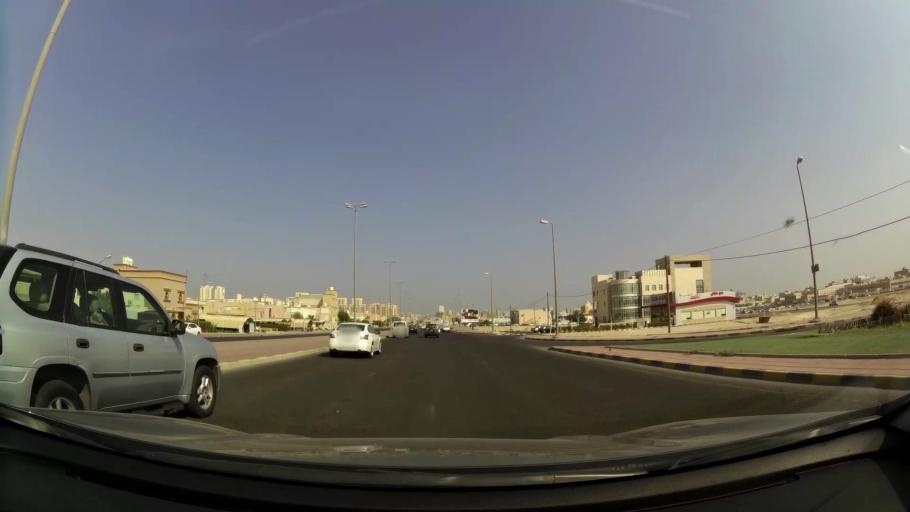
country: KW
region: Al Ahmadi
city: Ar Riqqah
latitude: 29.1348
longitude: 48.1065
